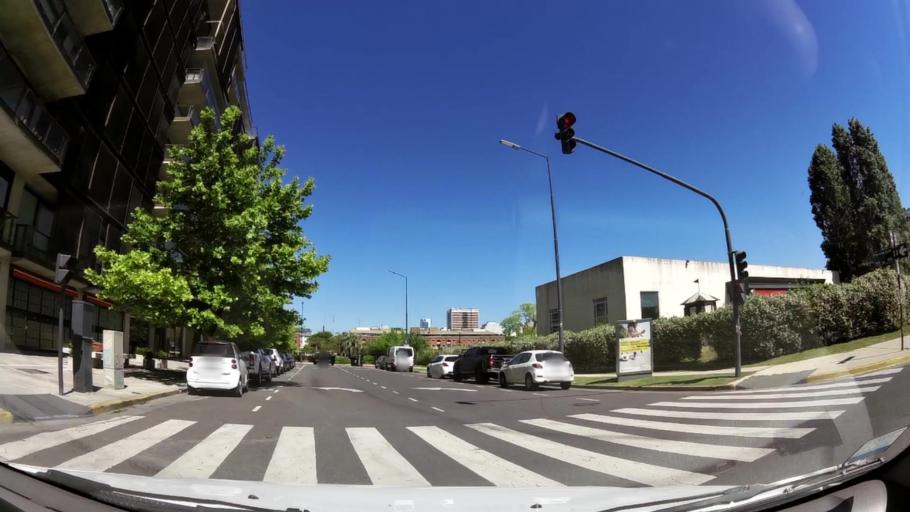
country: AR
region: Buenos Aires F.D.
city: Buenos Aires
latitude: -34.6149
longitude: -58.3623
